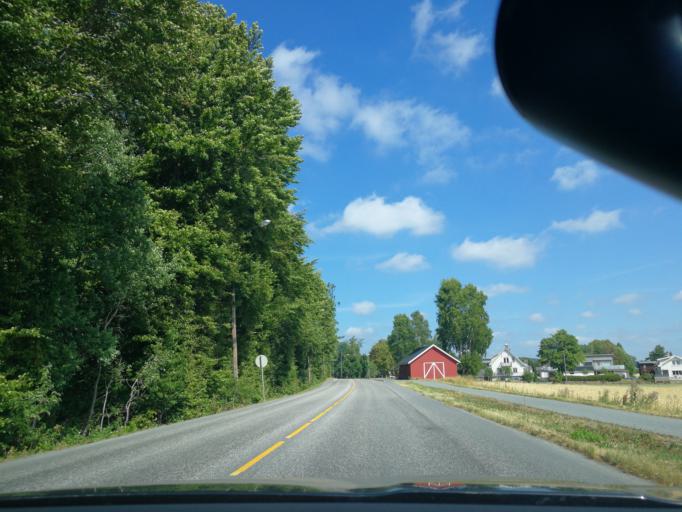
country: NO
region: Vestfold
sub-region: Sandefjord
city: Sandefjord
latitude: 59.1577
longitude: 10.1997
